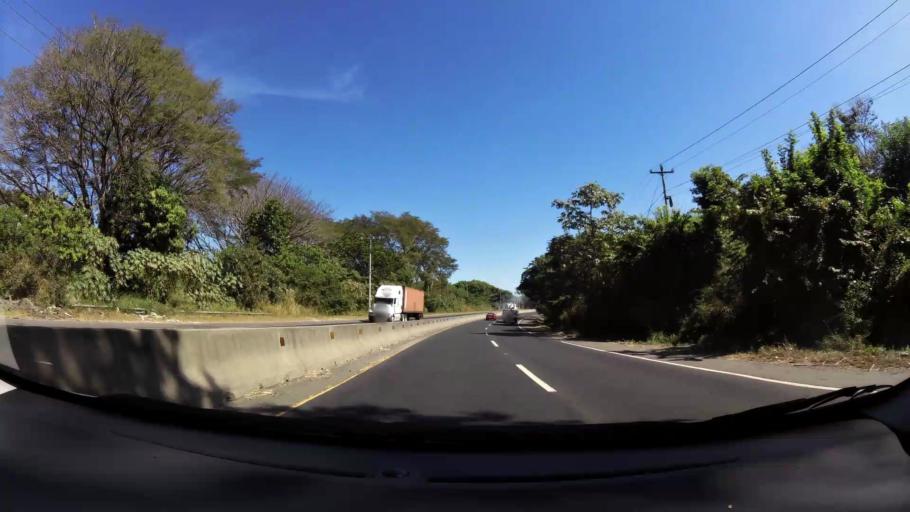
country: SV
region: La Libertad
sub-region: Distrito de Quezaltepeque
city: Quezaltepeque
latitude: 13.8213
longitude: -89.2899
